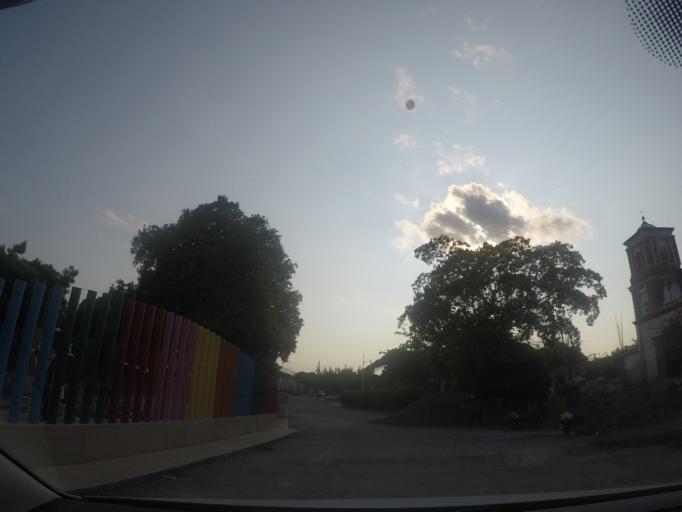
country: MX
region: Oaxaca
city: San Jeronimo Ixtepec
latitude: 16.5919
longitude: -95.1612
